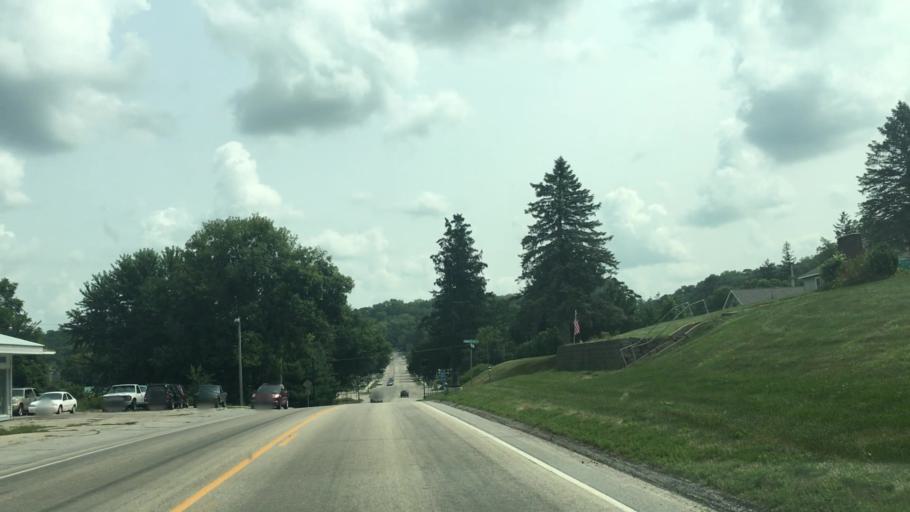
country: US
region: Minnesota
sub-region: Fillmore County
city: Preston
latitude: 43.7140
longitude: -91.9804
